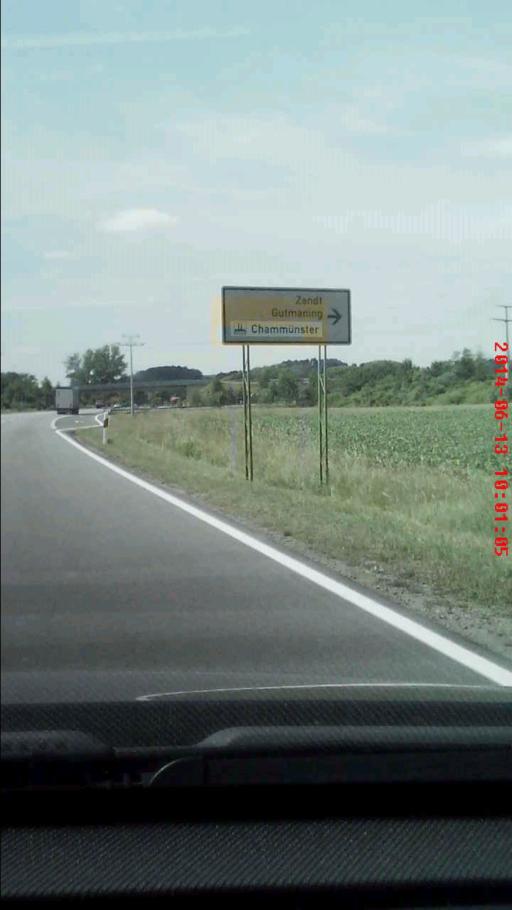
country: DE
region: Bavaria
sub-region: Upper Palatinate
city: Cham
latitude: 49.2096
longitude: 12.6777
